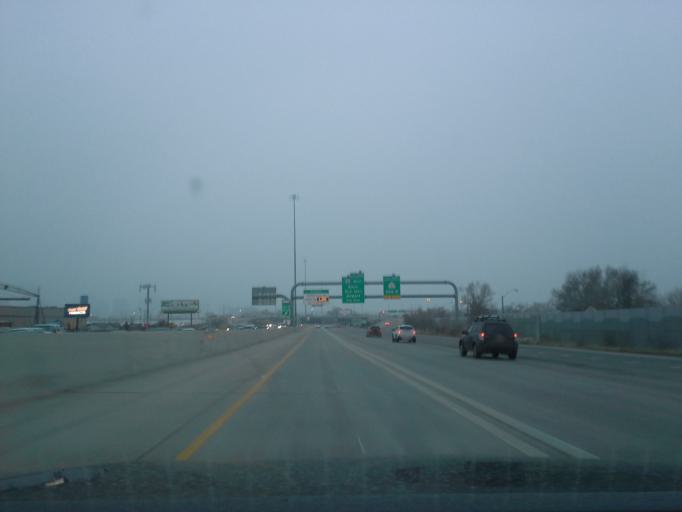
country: US
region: Utah
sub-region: Salt Lake County
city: Salt Lake City
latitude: 40.7870
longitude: -111.9137
